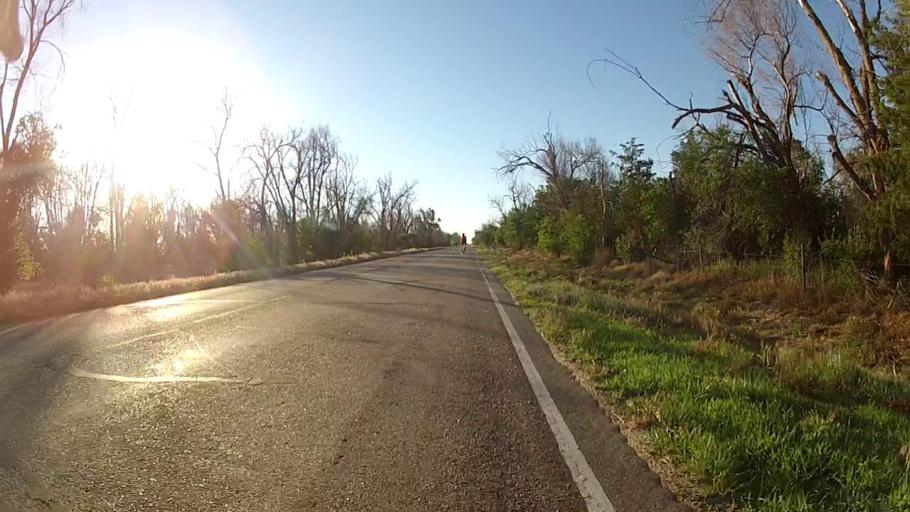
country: US
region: Kansas
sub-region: Ford County
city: Dodge City
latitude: 37.7128
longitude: -99.9256
